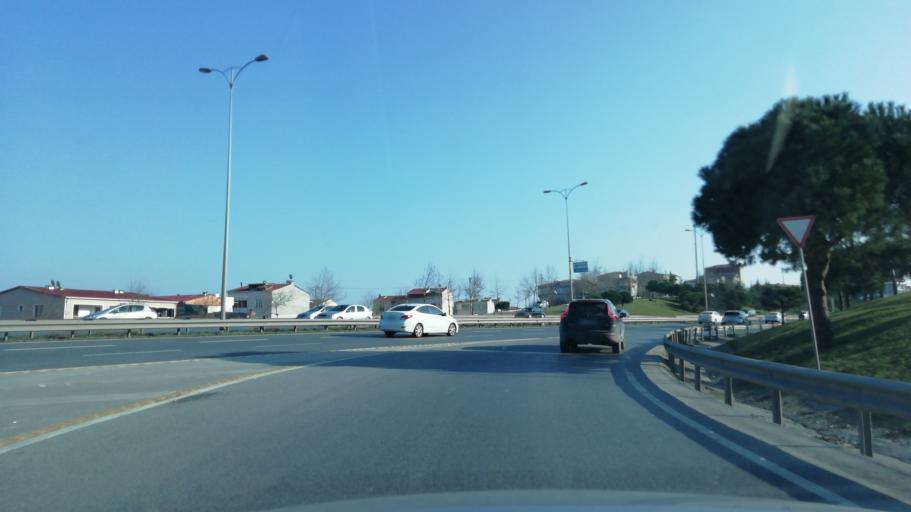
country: TR
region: Istanbul
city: Esenyurt
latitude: 41.0458
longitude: 28.6903
